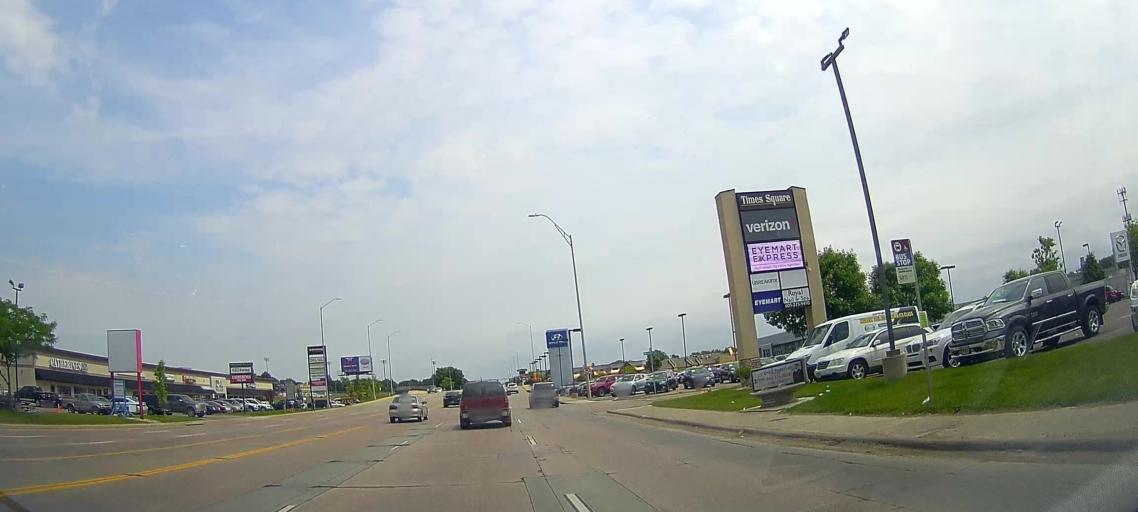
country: US
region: South Dakota
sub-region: Minnehaha County
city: Sioux Falls
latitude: 43.5148
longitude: -96.7687
